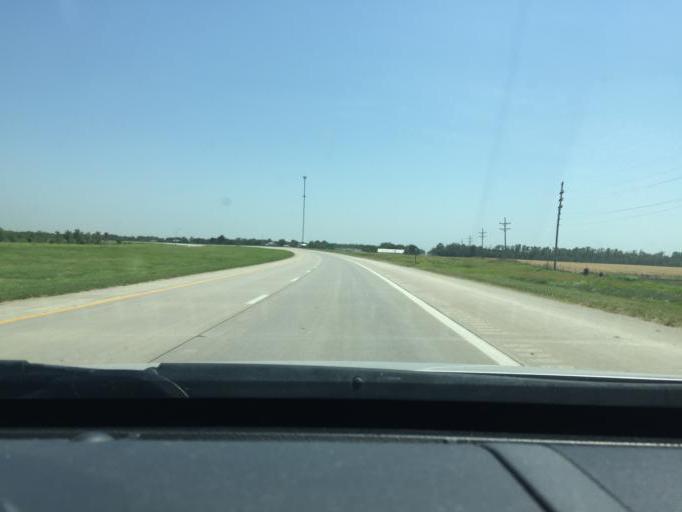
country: US
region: Kansas
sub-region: Reno County
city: South Hutchinson
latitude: 37.9783
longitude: -97.9404
